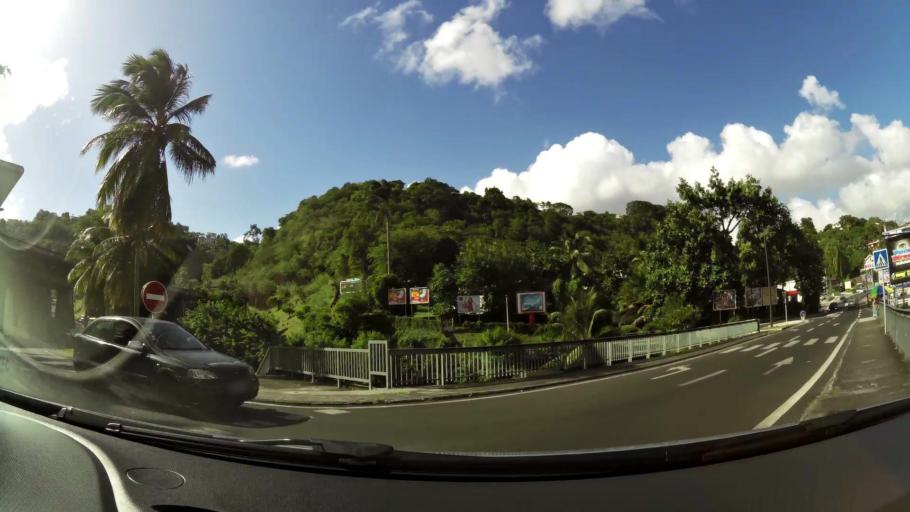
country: MQ
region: Martinique
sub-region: Martinique
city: Fort-de-France
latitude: 14.6169
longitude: -61.0713
